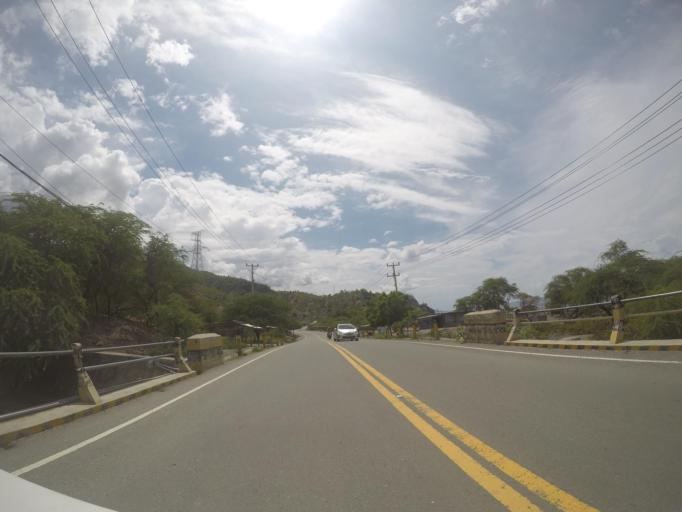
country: TL
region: Liquica
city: Liquica
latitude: -8.5715
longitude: 125.3794
